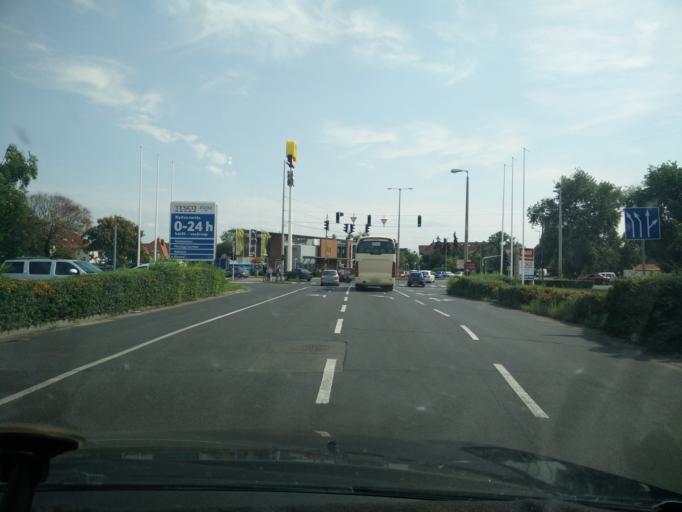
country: HU
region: Hajdu-Bihar
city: Debrecen
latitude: 47.5297
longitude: 21.6080
